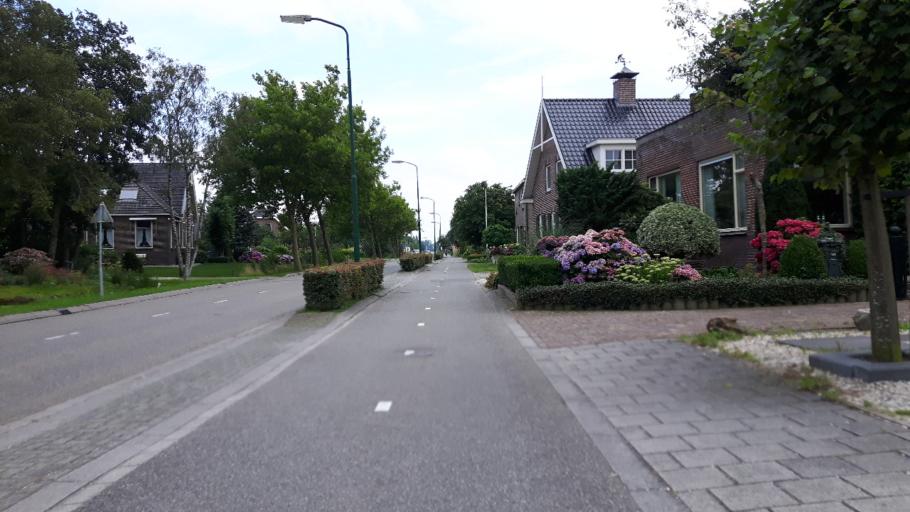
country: NL
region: Utrecht
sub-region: Gemeente Woerden
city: Woerden
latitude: 52.1100
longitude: 4.8443
